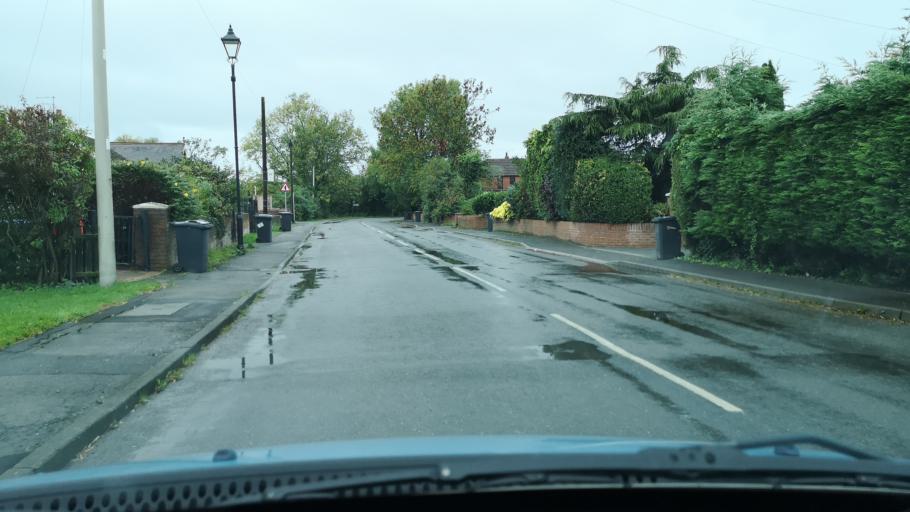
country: GB
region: England
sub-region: Doncaster
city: Stainforth
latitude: 53.6113
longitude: -1.0108
